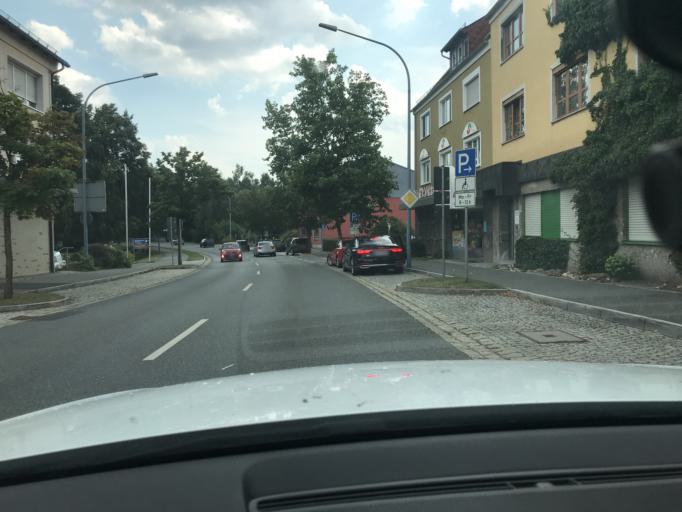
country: DE
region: Bavaria
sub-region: Upper Palatinate
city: Grafenwohr
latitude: 49.7210
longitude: 11.9025
